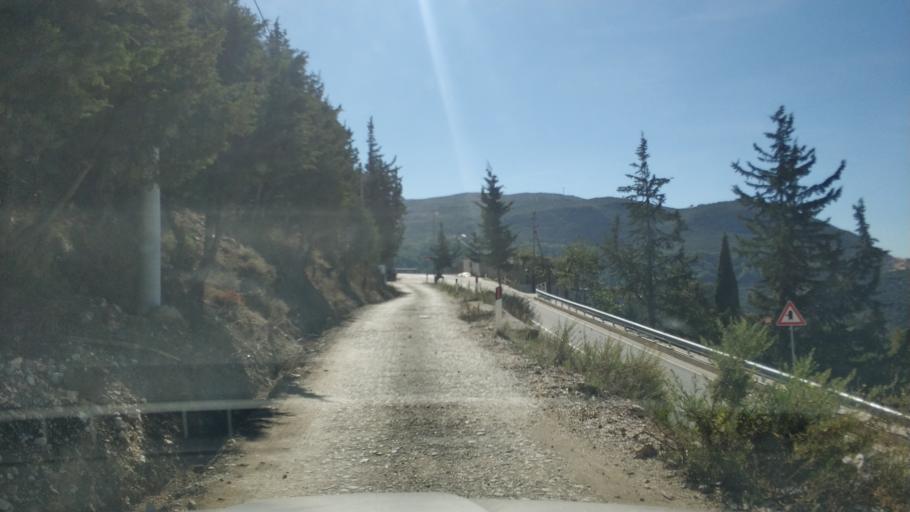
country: AL
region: Vlore
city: Vlore
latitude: 40.4450
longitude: 19.5185
